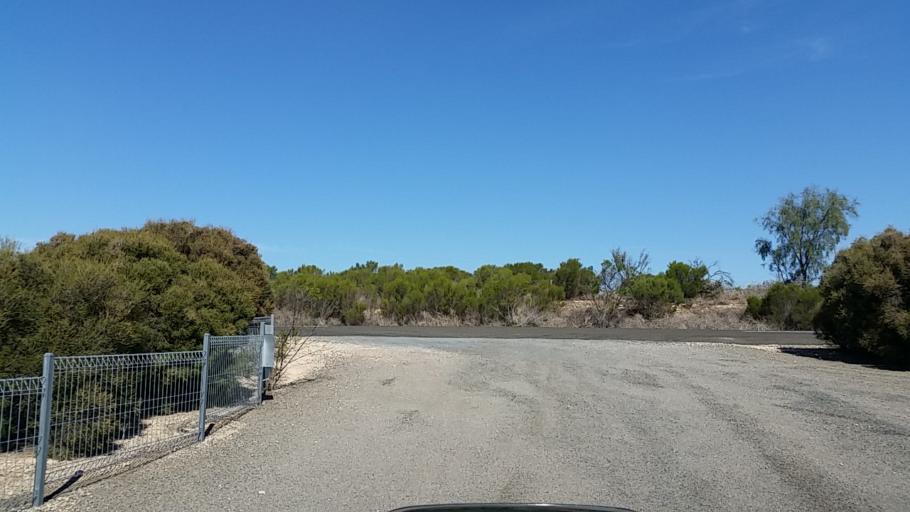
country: AU
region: South Australia
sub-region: Mid Murray
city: Mannum
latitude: -34.7463
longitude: 139.5424
